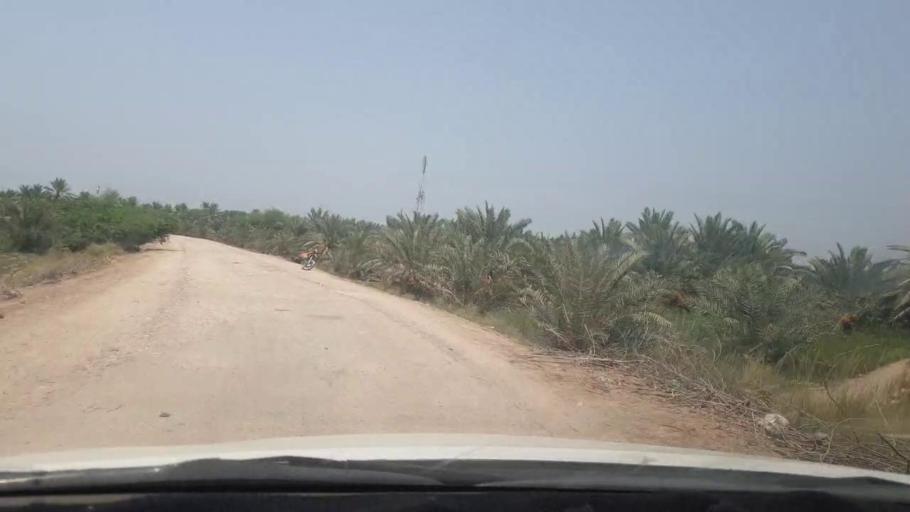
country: PK
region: Sindh
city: Khairpur
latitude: 27.5051
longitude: 68.8629
